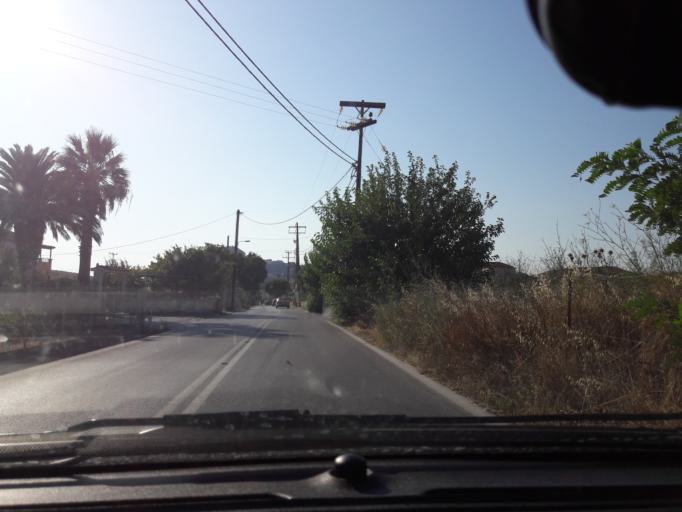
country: GR
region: North Aegean
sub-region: Nomos Lesvou
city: Myrina
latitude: 39.8710
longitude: 25.0686
